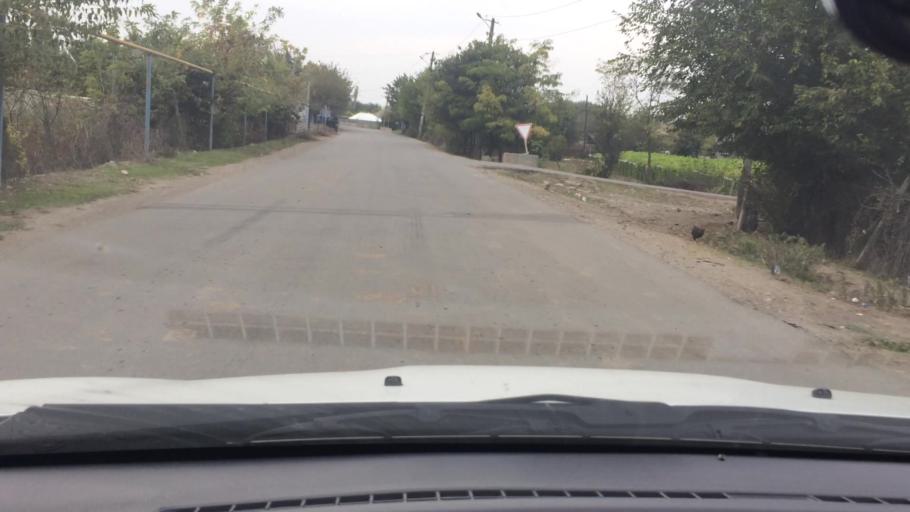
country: AM
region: Tavush
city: Berdavan
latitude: 41.3531
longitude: 44.9668
